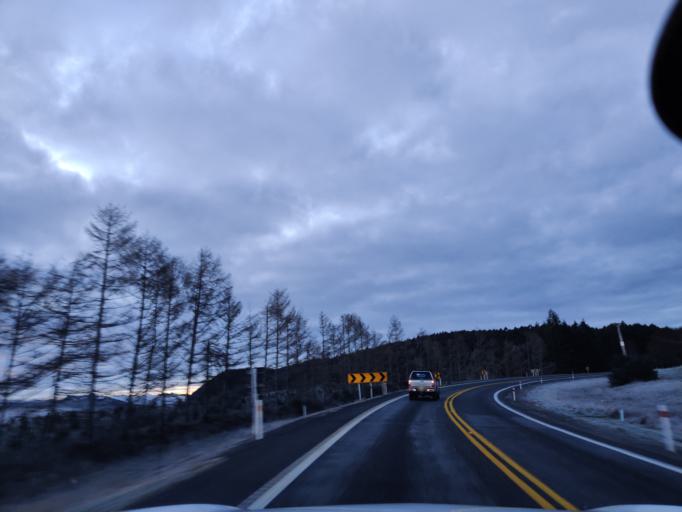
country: NZ
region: Waikato
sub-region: South Waikato District
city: Tokoroa
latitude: -38.4012
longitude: 176.0499
